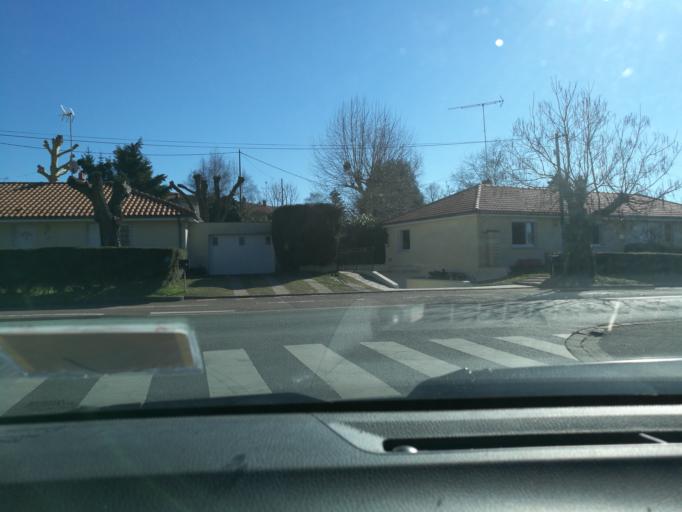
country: FR
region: Centre
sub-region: Departement du Loiret
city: Saint-Jean-de-la-Ruelle
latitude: 47.8989
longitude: 1.8651
